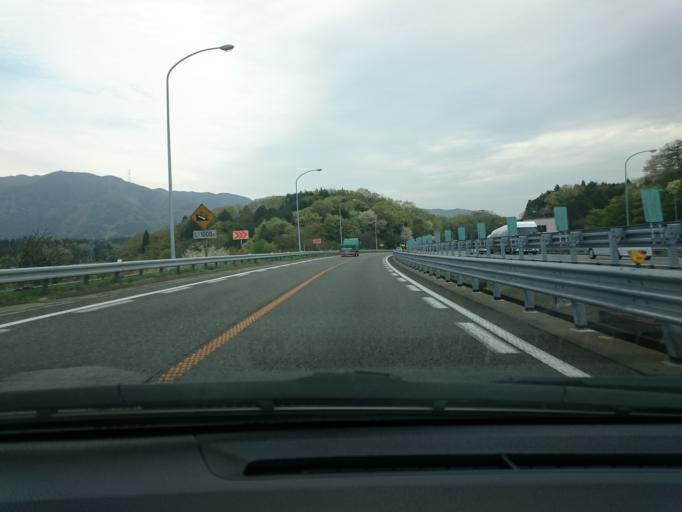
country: JP
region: Gifu
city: Tarui
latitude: 35.3524
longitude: 136.4466
